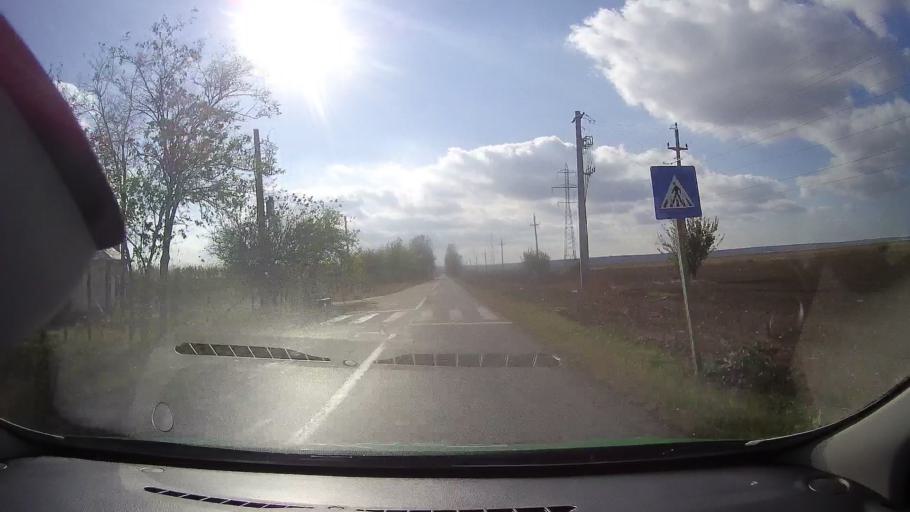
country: RO
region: Constanta
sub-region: Comuna Istria
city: Istria
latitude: 44.5459
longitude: 28.6925
